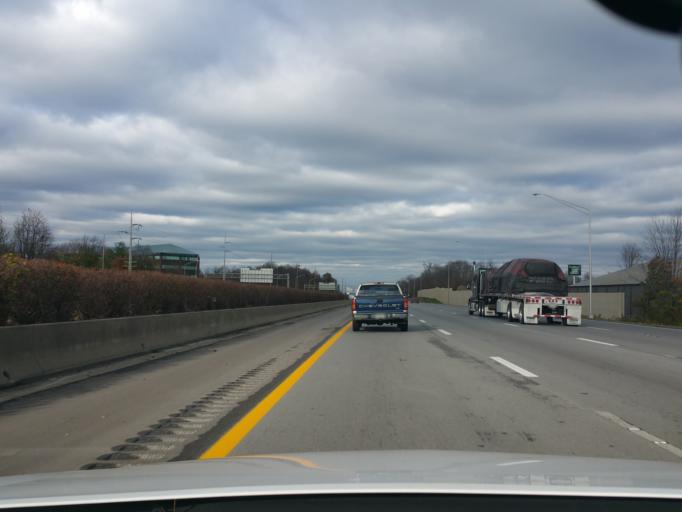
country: US
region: Kentucky
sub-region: Jefferson County
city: Hurstbourne Acres
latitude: 38.2248
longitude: -85.5833
